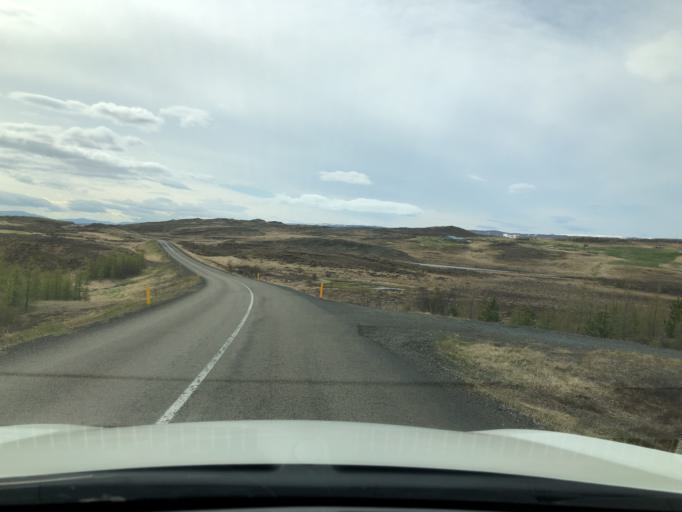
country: IS
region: East
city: Egilsstadir
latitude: 65.2688
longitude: -14.4690
